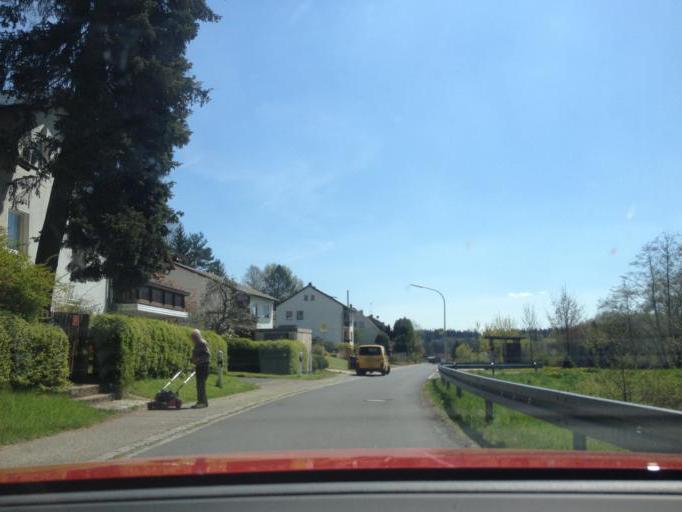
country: DE
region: Bavaria
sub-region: Upper Franconia
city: Thiersheim
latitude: 50.0543
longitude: 12.1058
